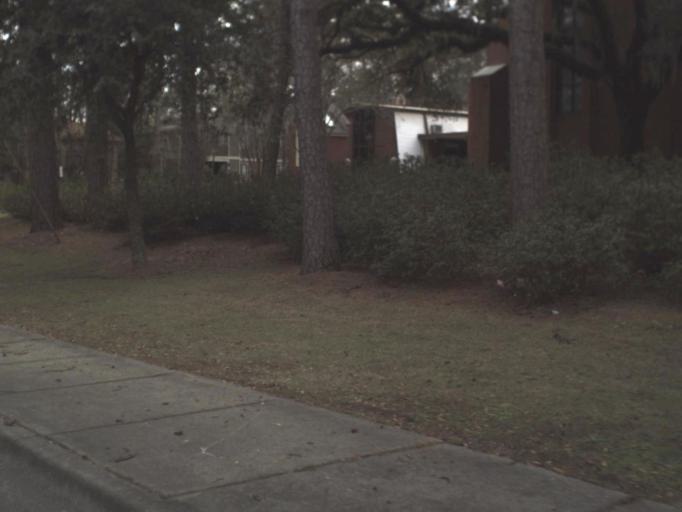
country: US
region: Florida
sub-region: Leon County
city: Tallahassee
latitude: 30.4725
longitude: -84.2773
